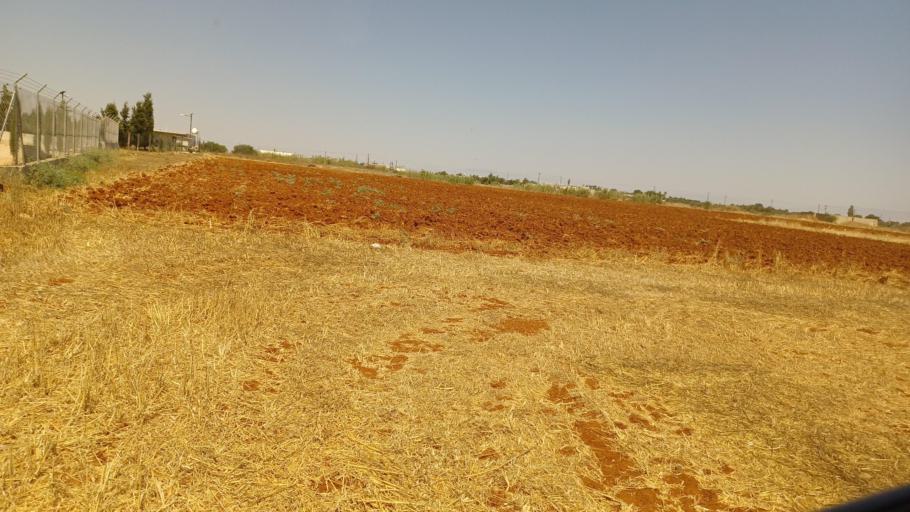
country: CY
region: Ammochostos
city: Frenaros
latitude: 35.0682
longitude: 33.8924
